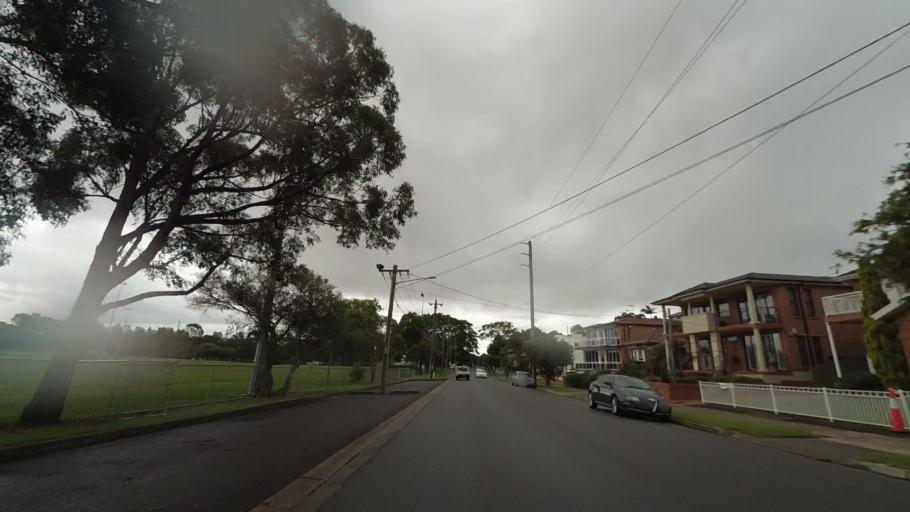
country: AU
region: New South Wales
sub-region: Rockdale
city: Ramsgate
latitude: -33.9853
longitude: 151.1323
